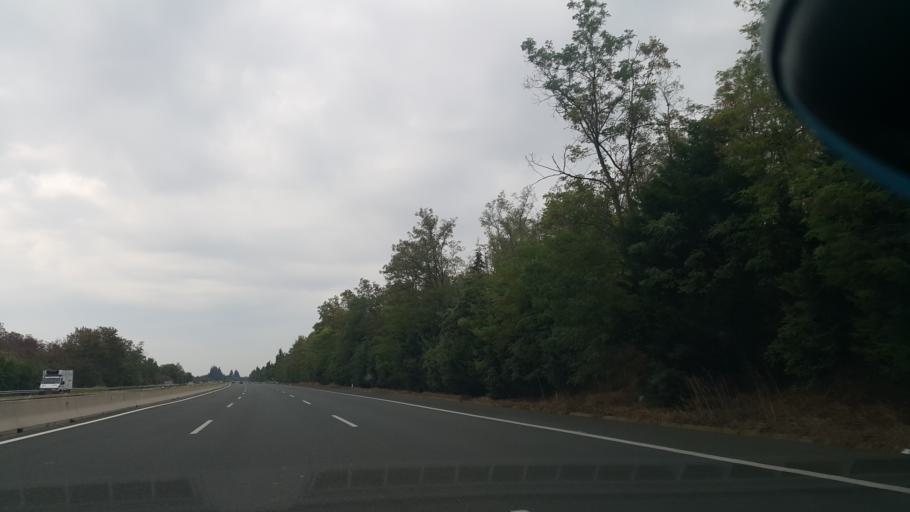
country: GR
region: Central Macedonia
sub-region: Nomos Pierias
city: Makrygialos
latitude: 40.4055
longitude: 22.5957
